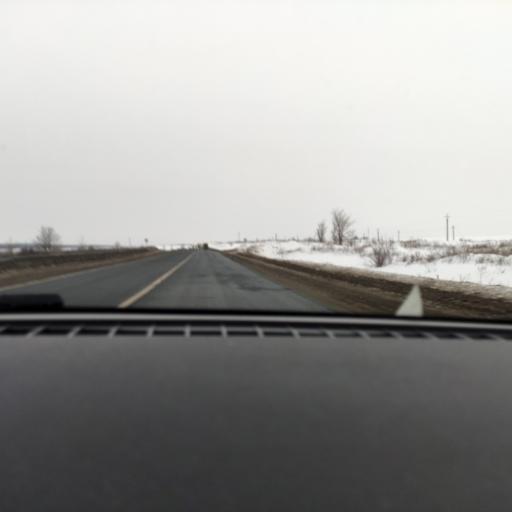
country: RU
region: Samara
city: Smyshlyayevka
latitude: 53.2862
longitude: 50.4611
